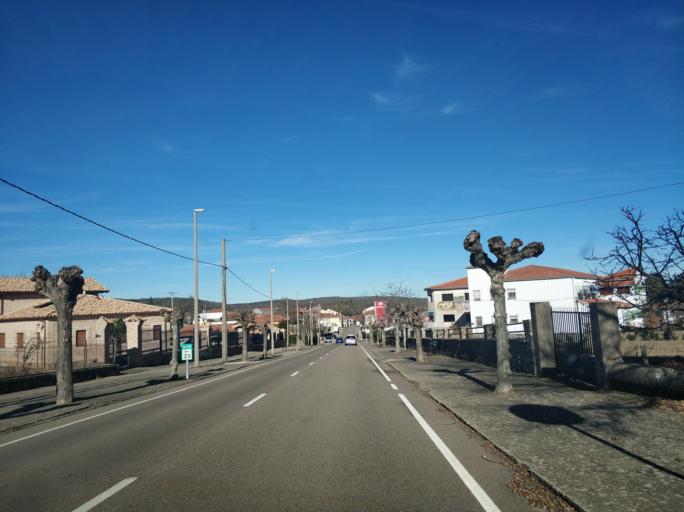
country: ES
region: Castille and Leon
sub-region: Provincia de Salamanca
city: Linares de Riofrio
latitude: 40.5782
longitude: -5.9186
